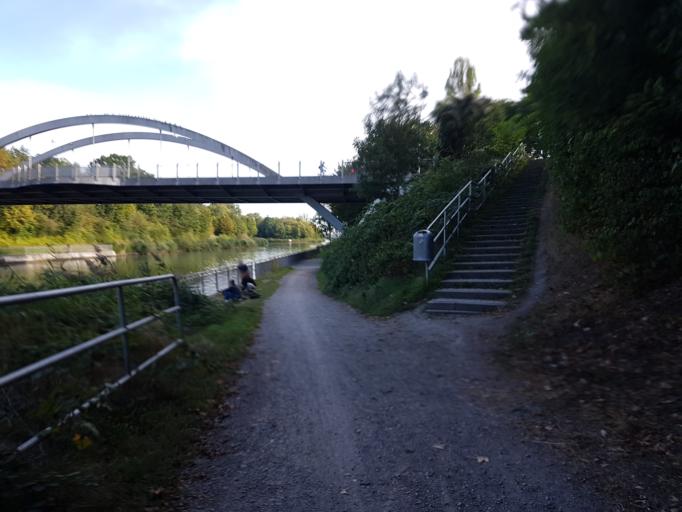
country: DE
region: Lower Saxony
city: Laatzen
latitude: 52.3872
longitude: 9.8342
